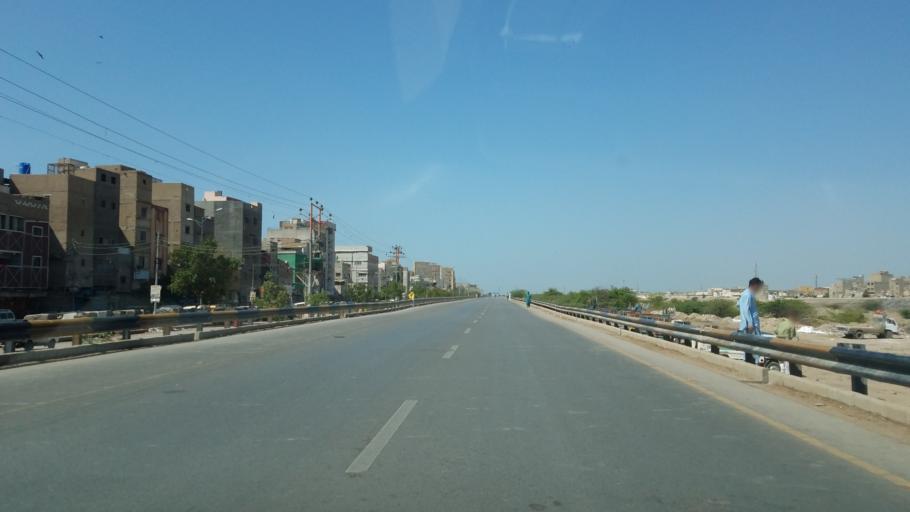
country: PK
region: Sindh
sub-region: Karachi District
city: Karachi
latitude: 24.8783
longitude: 66.9918
